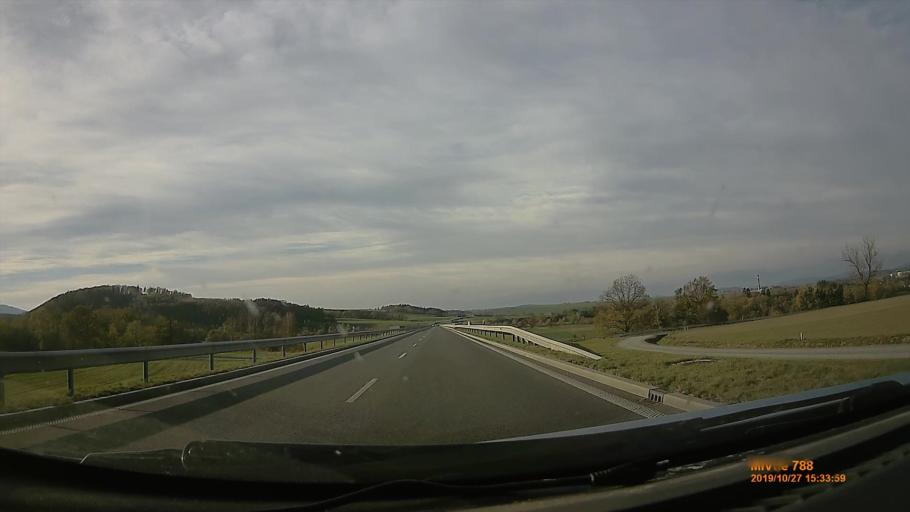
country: PL
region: Lower Silesian Voivodeship
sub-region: Powiat klodzki
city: Klodzko
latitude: 50.4018
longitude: 16.6468
